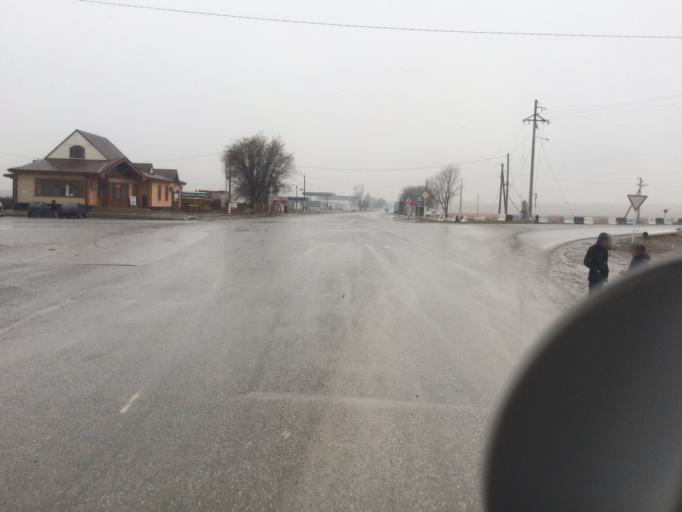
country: KG
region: Chuy
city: Kant
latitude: 43.0009
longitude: 74.8673
